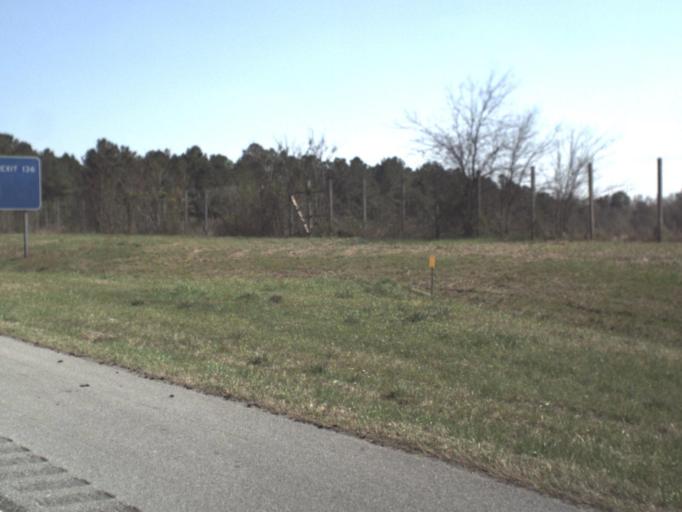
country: US
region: Florida
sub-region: Jackson County
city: Marianna
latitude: 30.7570
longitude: -85.2824
